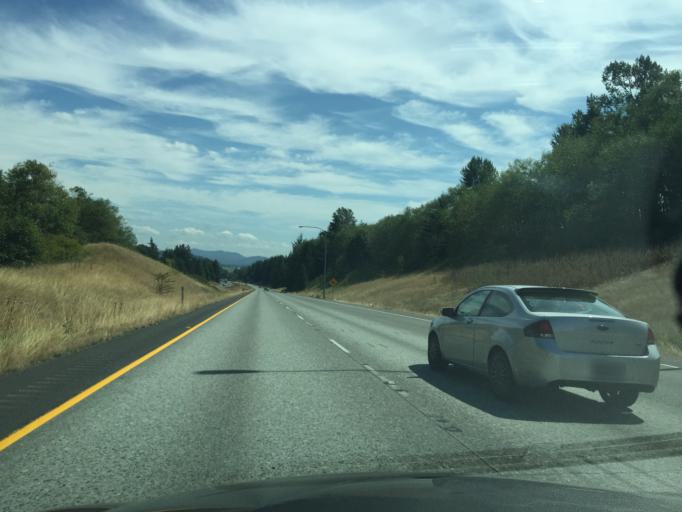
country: US
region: Washington
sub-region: Skagit County
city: Burlington
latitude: 48.5330
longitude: -122.3530
